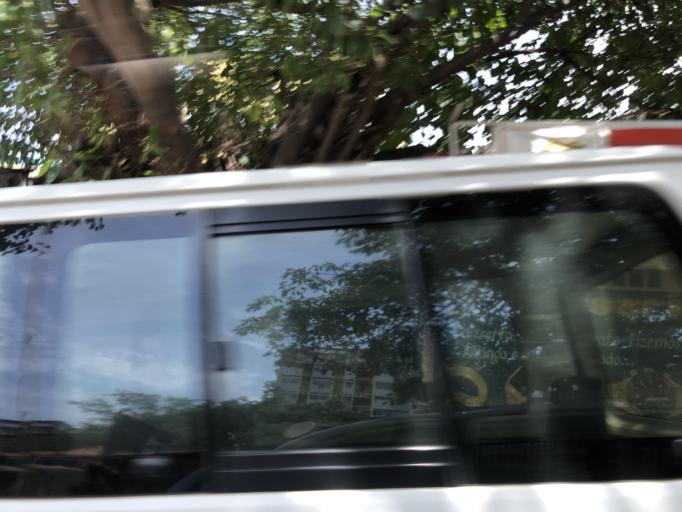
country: AO
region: Luanda
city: Luanda
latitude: -8.8210
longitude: 13.2312
